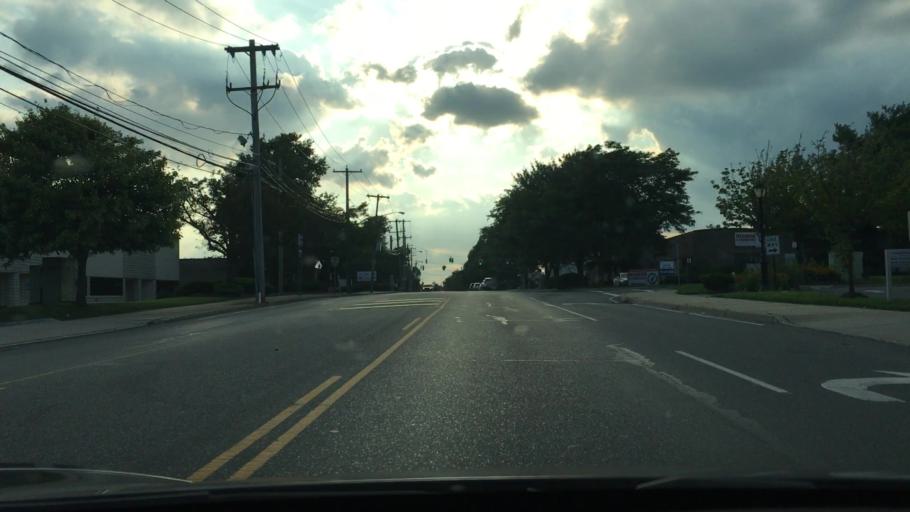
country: US
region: New York
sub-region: Suffolk County
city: Bay Wood
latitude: 40.7608
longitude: -73.2966
